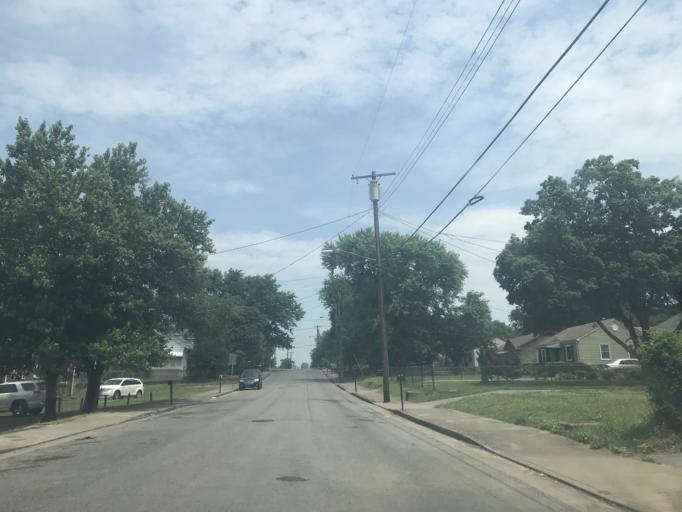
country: US
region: Tennessee
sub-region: Davidson County
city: Nashville
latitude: 36.1812
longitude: -86.8177
